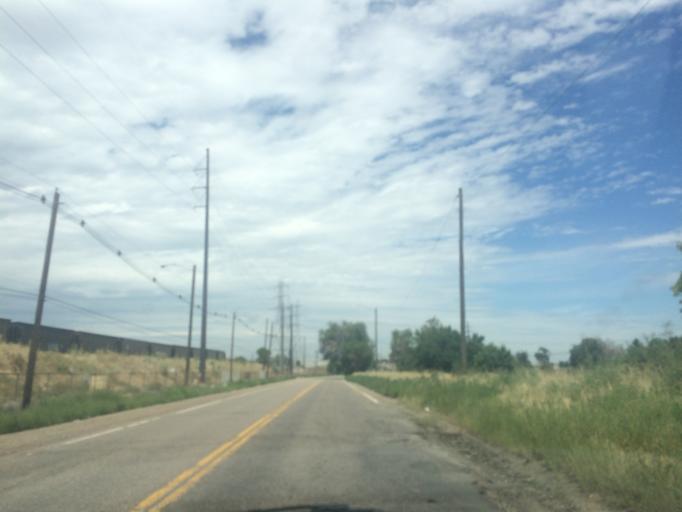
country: US
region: Colorado
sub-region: Adams County
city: Commerce City
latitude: 39.8094
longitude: -104.9599
